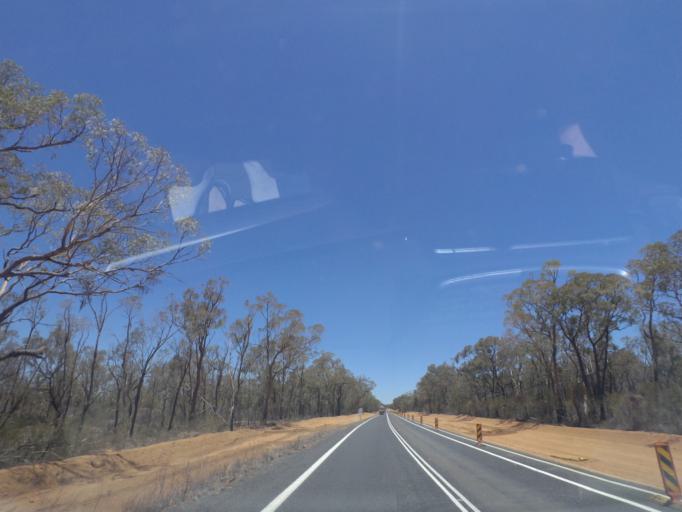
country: AU
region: New South Wales
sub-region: Warrumbungle Shire
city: Coonabarabran
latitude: -30.9260
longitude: 149.4309
